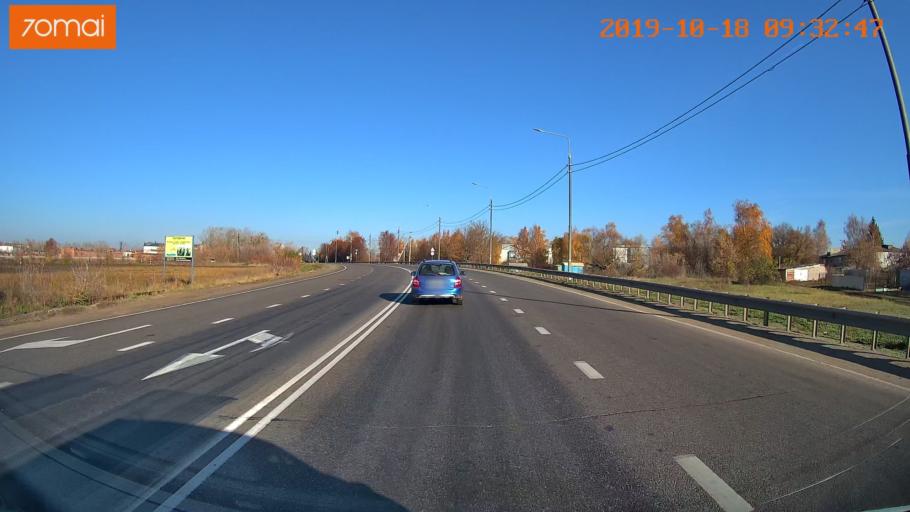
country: RU
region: Tula
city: Yefremov
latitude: 53.1614
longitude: 38.1549
